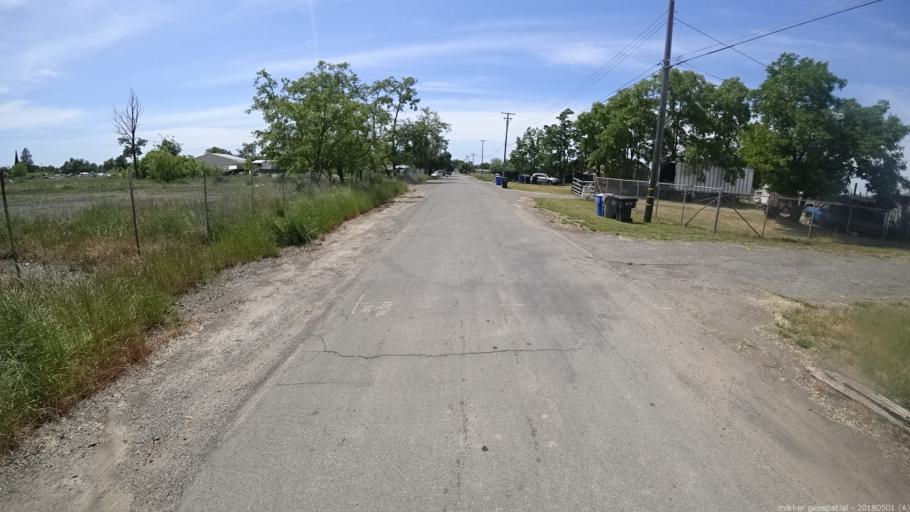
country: US
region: California
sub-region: Sacramento County
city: Rio Linda
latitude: 38.6619
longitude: -121.4352
